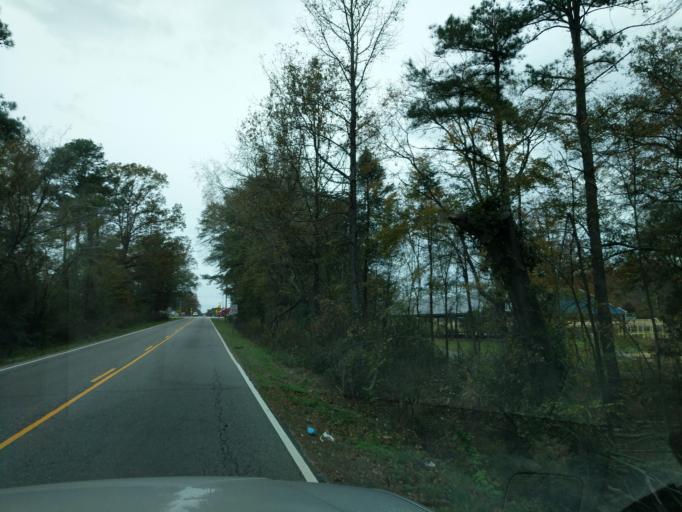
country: US
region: South Carolina
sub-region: Lexington County
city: Batesburg
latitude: 33.9533
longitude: -81.6345
